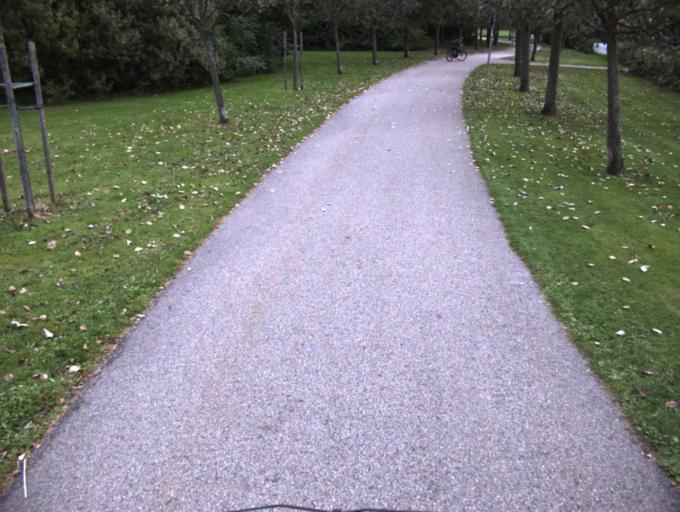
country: SE
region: Skane
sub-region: Helsingborg
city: Odakra
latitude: 56.0965
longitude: 12.7543
